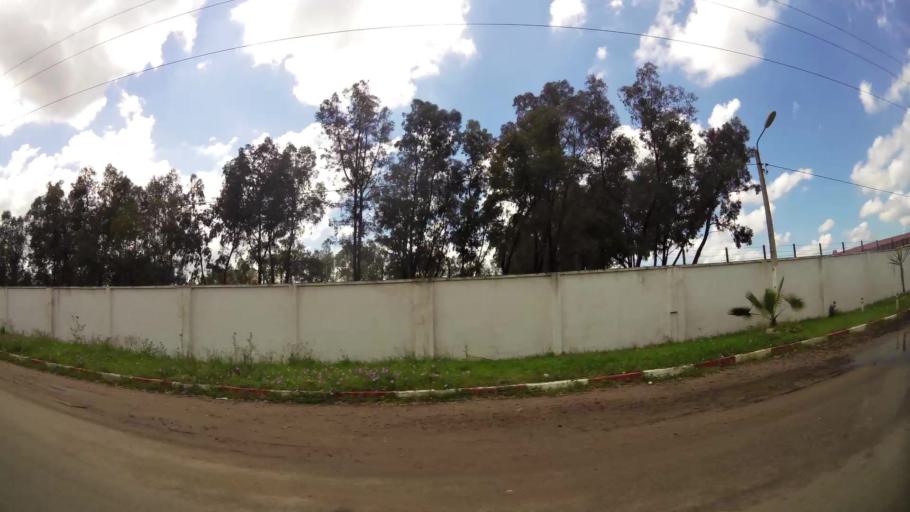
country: MA
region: Chaouia-Ouardigha
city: Nouaseur
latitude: 33.3917
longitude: -7.5776
